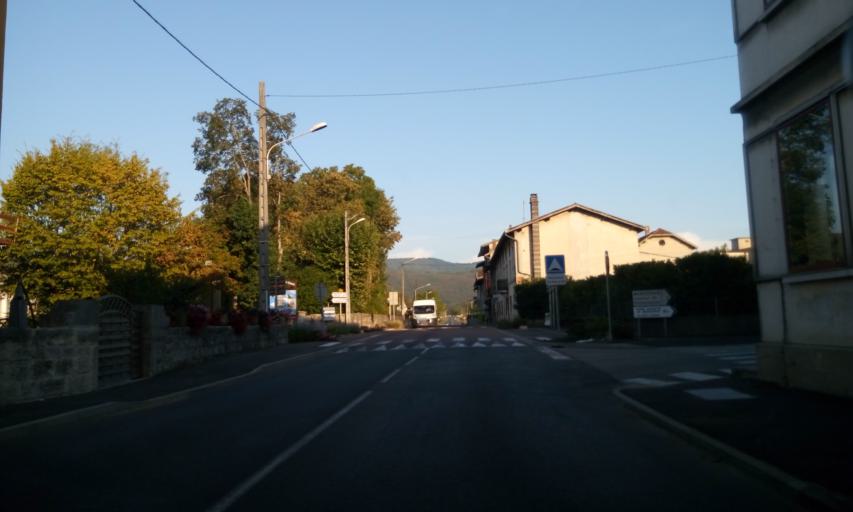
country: FR
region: Rhone-Alpes
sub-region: Departement de l'Ain
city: Poncin
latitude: 46.0828
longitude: 5.4063
